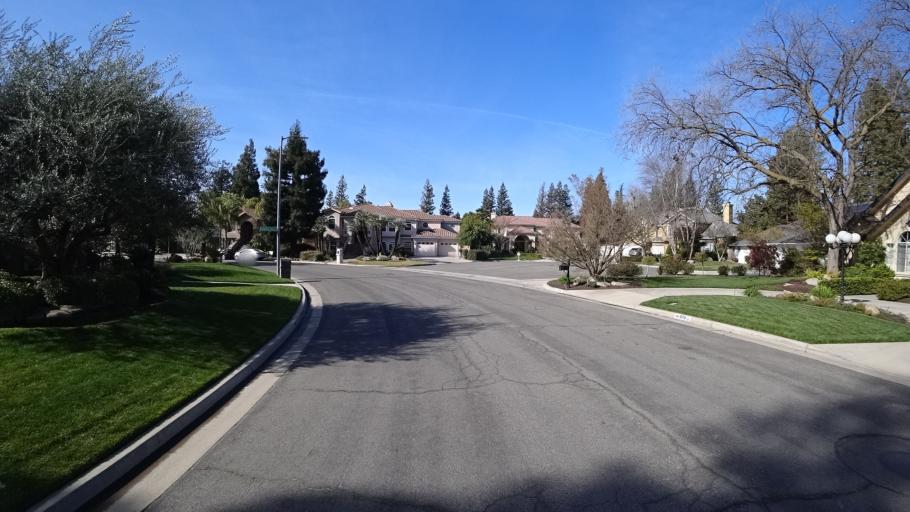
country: US
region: California
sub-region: Fresno County
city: Clovis
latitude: 36.8903
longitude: -119.7674
